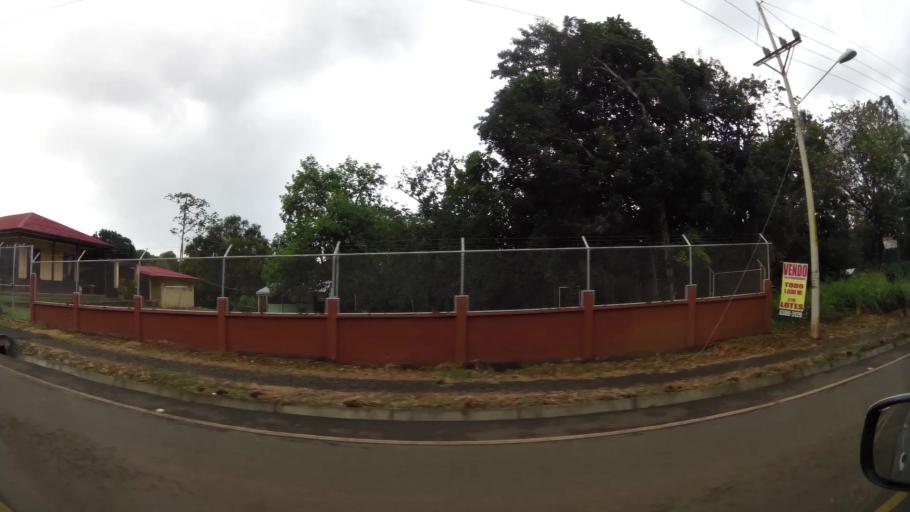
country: CR
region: Alajuela
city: Orotina
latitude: 9.9593
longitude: -84.5903
